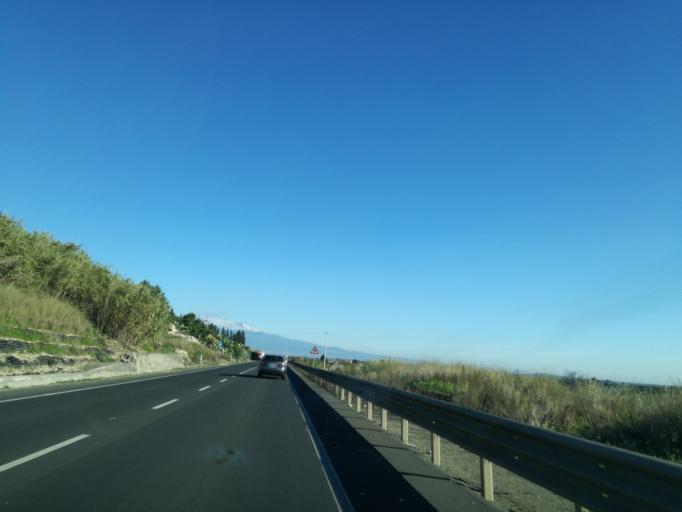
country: IT
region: Sicily
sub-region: Catania
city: Ramacca
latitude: 37.3708
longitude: 14.7243
